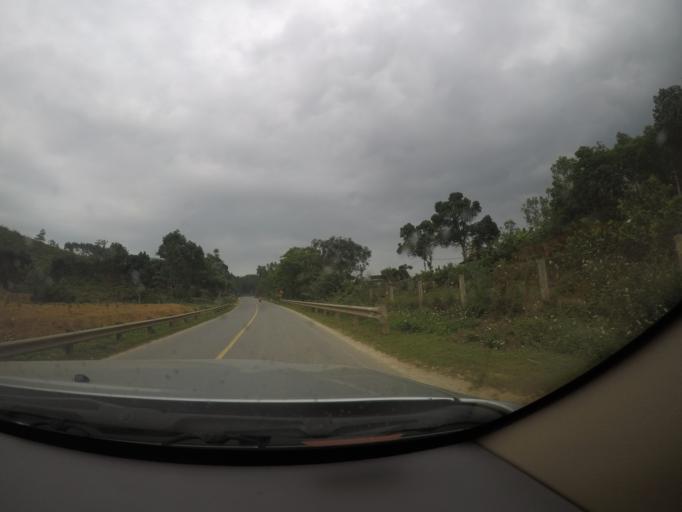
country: VN
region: Quang Binh
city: Ba Don
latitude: 17.6166
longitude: 106.3740
